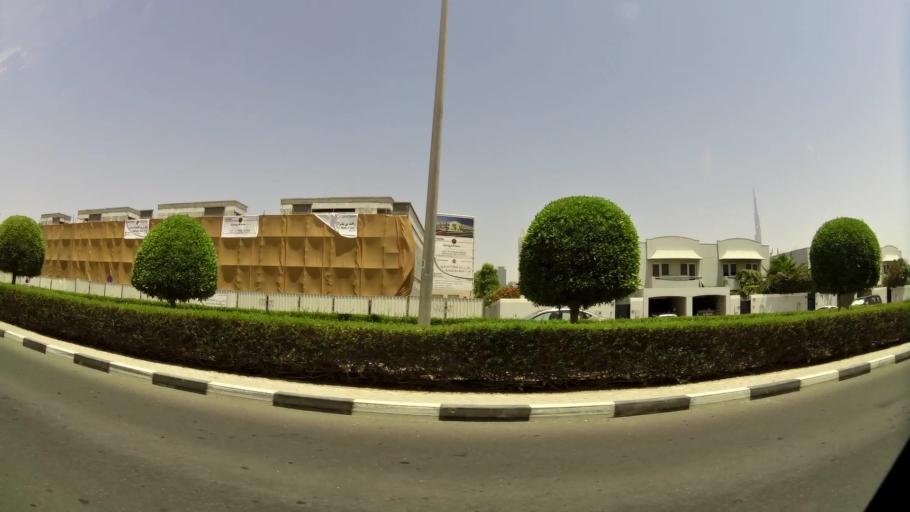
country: AE
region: Dubai
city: Dubai
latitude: 25.2217
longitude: 55.2635
